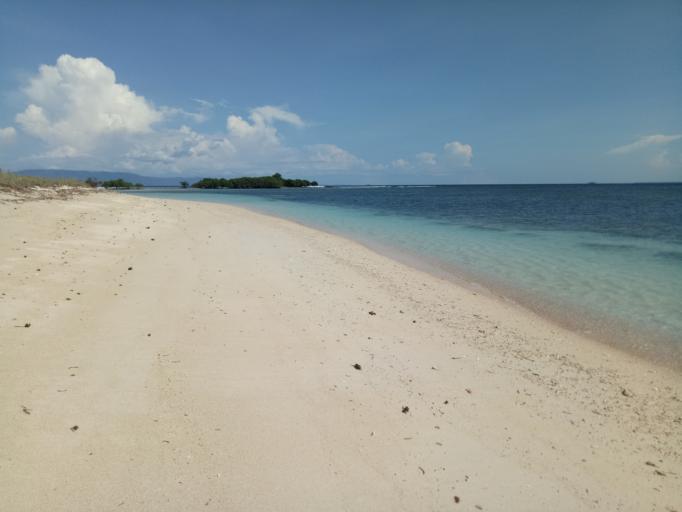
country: ID
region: West Nusa Tenggara
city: Sambelia
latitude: -8.4470
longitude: 116.7307
